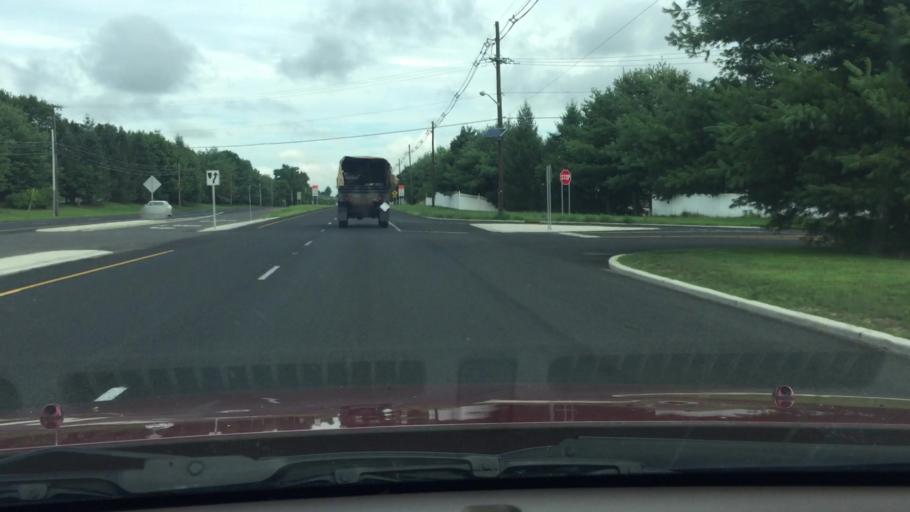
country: US
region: New Jersey
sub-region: Burlington County
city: Fort Dix
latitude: 40.0806
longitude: -74.6665
